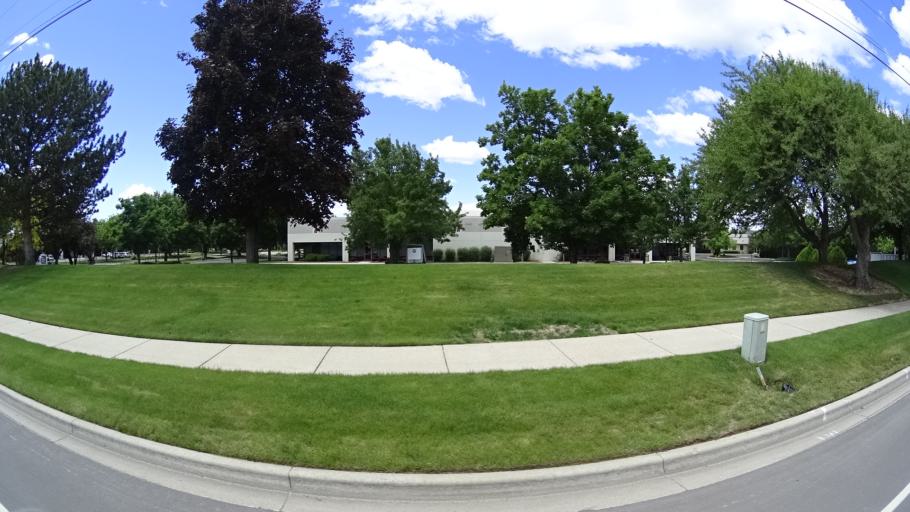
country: US
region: Idaho
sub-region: Ada County
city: Eagle
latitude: 43.6601
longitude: -116.3345
